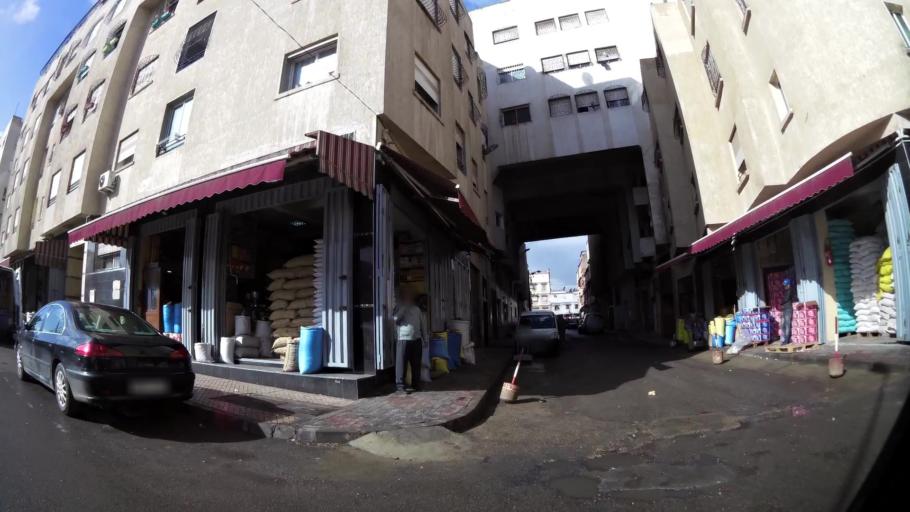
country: MA
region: Grand Casablanca
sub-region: Casablanca
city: Casablanca
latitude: 33.5699
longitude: -7.5814
